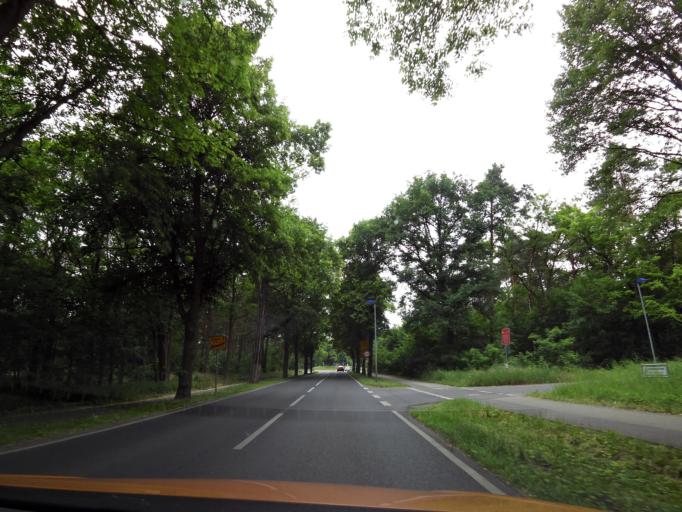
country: DE
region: Brandenburg
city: Zossen
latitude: 52.1738
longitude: 13.4694
